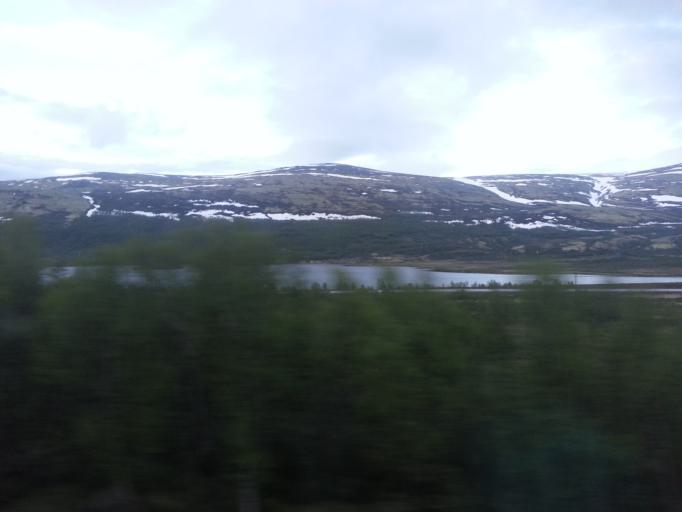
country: NO
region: Oppland
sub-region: Dovre
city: Dovre
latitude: 62.1784
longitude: 9.4587
